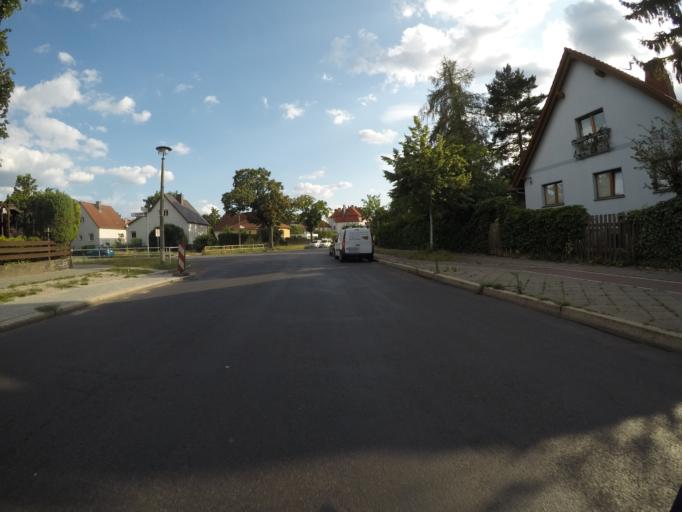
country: DE
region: Berlin
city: Kaulsdorf
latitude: 52.5157
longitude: 13.5931
